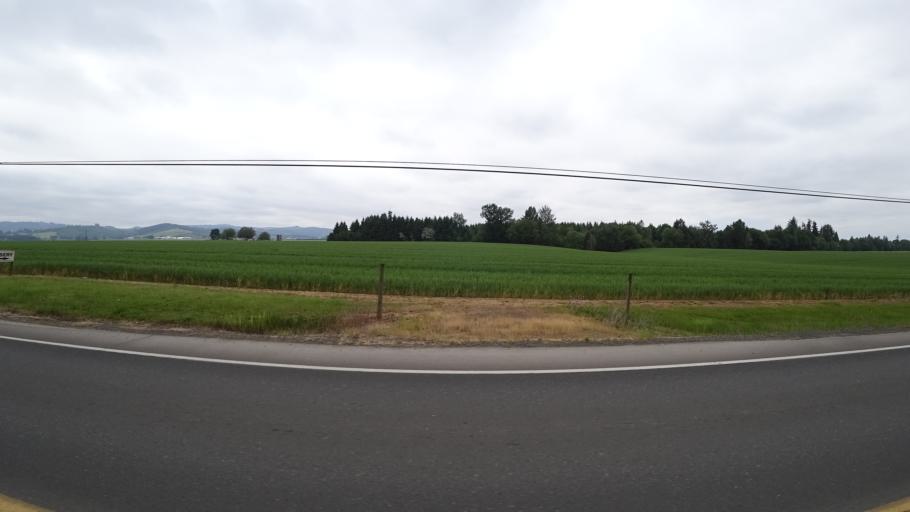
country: US
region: Oregon
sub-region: Washington County
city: Hillsboro
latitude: 45.4871
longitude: -122.9911
